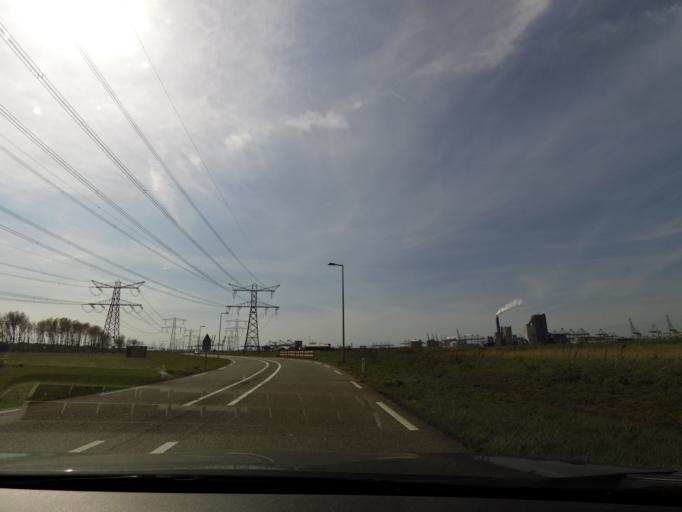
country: NL
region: South Holland
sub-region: Gemeente Rotterdam
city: Hoek van Holland
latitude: 51.9356
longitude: 4.0863
